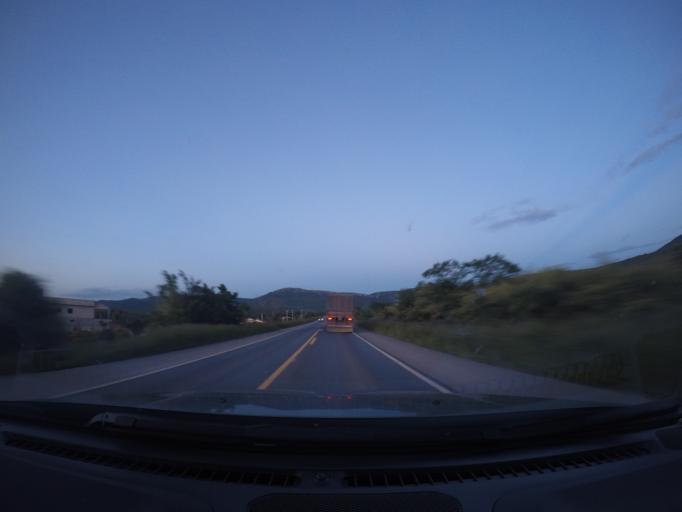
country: BR
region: Bahia
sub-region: Seabra
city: Seabra
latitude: -12.4815
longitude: -41.7195
